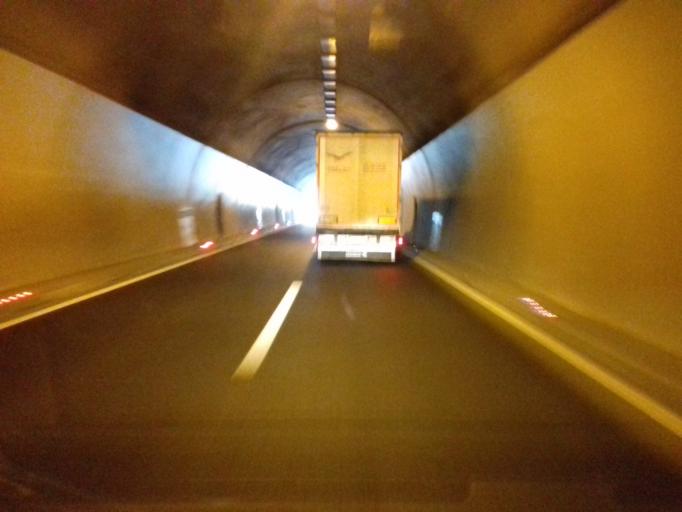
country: BA
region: Federation of Bosnia and Herzegovina
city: Vogosca
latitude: 43.8929
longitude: 18.3181
